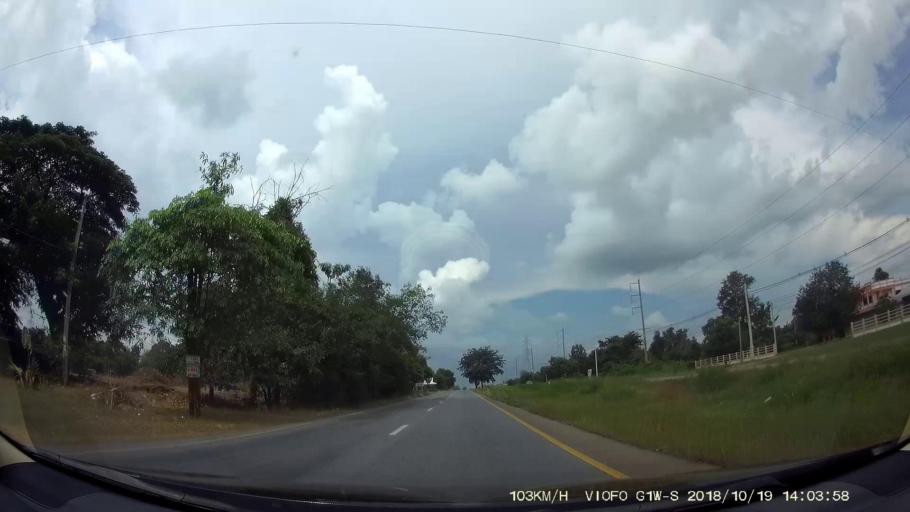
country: TH
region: Chaiyaphum
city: Chaiyaphum
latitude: 15.8579
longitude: 102.0759
